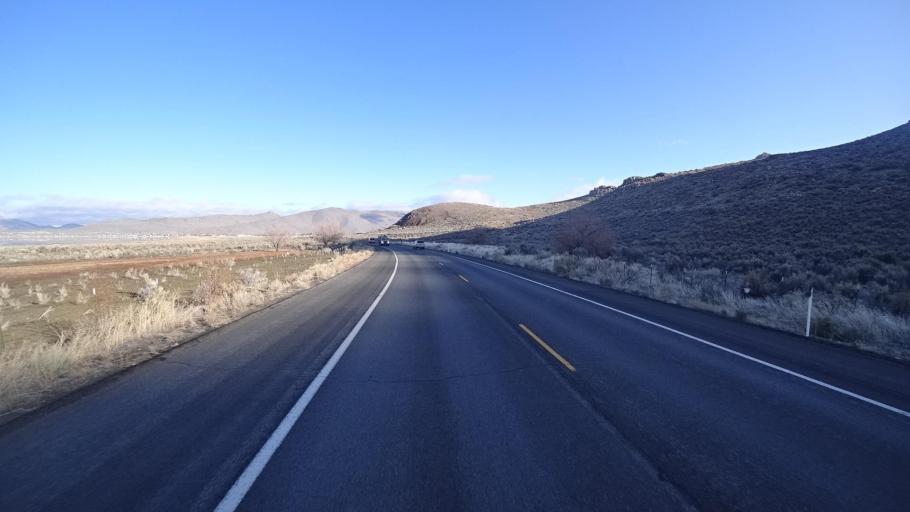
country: US
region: Nevada
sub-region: Washoe County
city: Cold Springs
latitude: 39.6582
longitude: -119.9585
